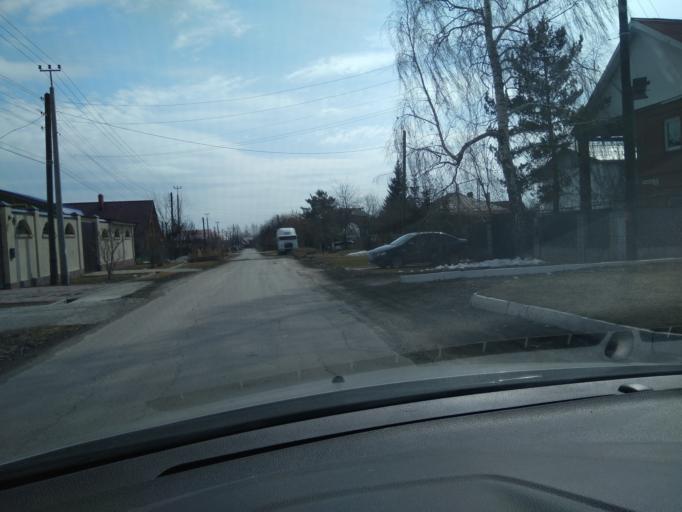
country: RU
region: Sverdlovsk
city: Shuvakish
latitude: 56.8902
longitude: 60.4852
